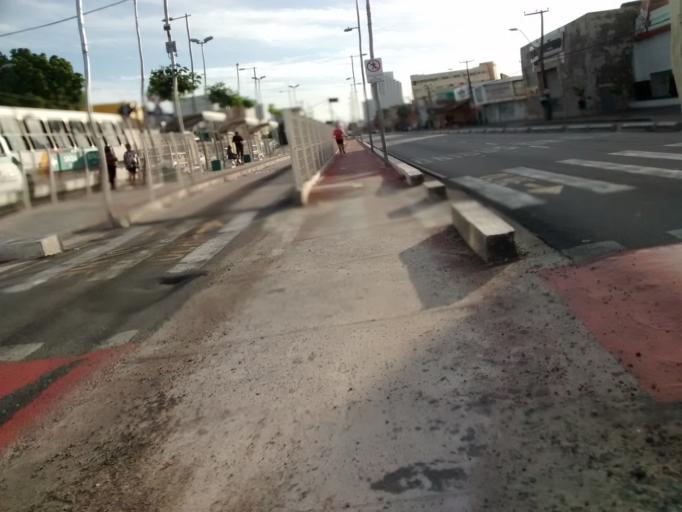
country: BR
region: Ceara
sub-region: Fortaleza
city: Fortaleza
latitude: -3.7323
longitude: -38.5484
